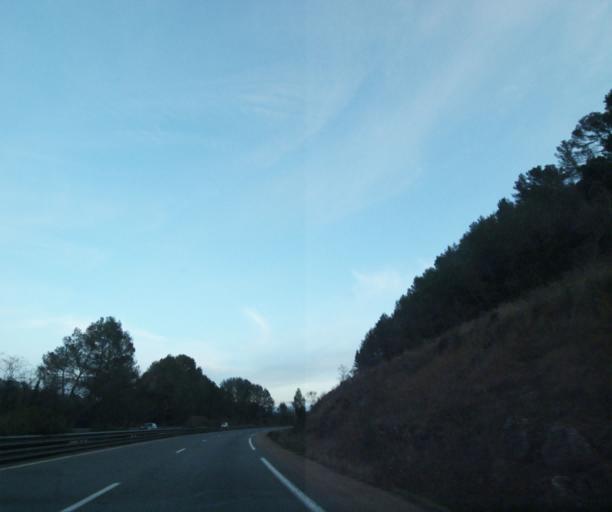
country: FR
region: Provence-Alpes-Cote d'Azur
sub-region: Departement du Var
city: Trans-en-Provence
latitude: 43.4934
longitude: 6.5031
